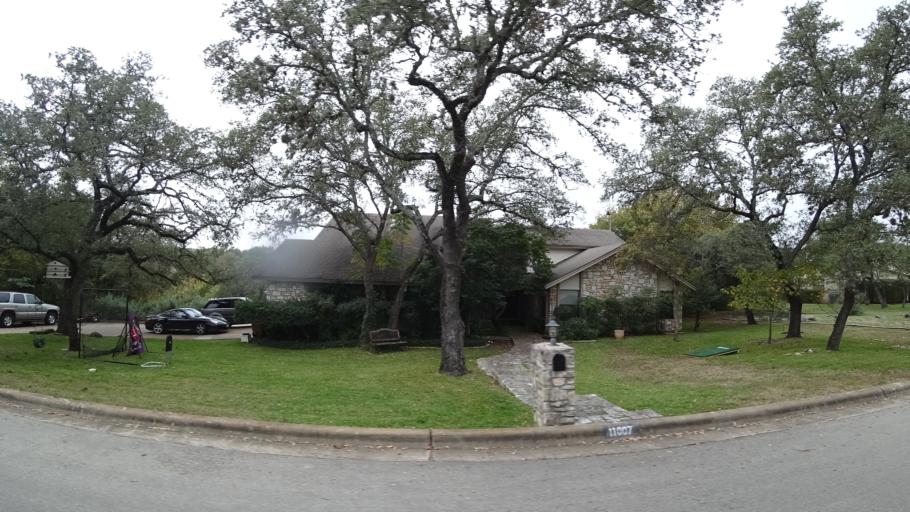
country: US
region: Texas
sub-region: Williamson County
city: Anderson Mill
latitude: 30.4424
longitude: -97.8175
